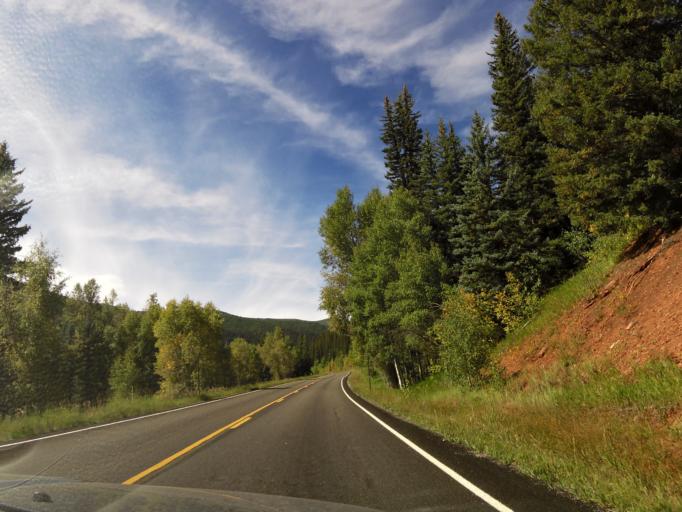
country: US
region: Colorado
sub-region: Montezuma County
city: Mancos
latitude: 37.5991
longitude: -108.1174
